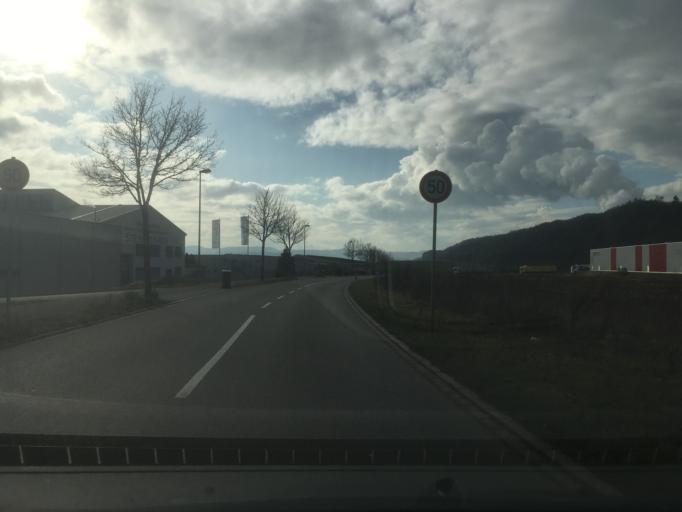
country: CH
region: Aargau
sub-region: Bezirk Zurzach
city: Koblenz
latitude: 47.6247
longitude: 8.2517
